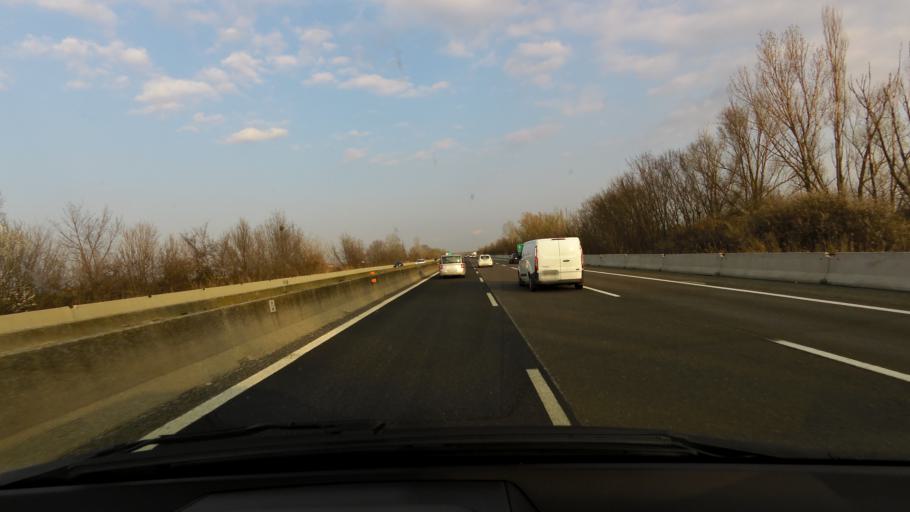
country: IT
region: Emilia-Romagna
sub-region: Provincia di Bologna
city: Osteria Grande
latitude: 44.4581
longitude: 11.5153
